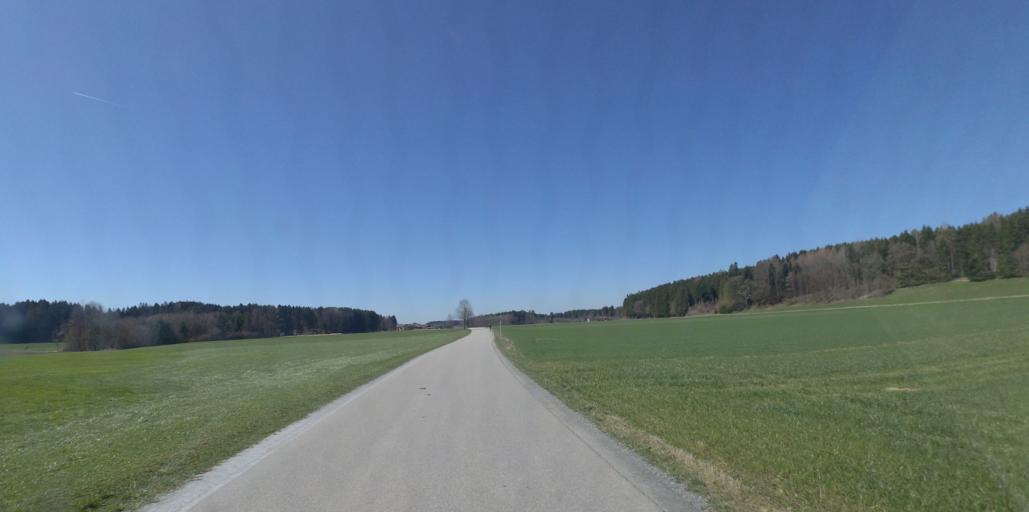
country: DE
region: Bavaria
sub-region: Upper Bavaria
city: Chieming
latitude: 47.9122
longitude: 12.5554
